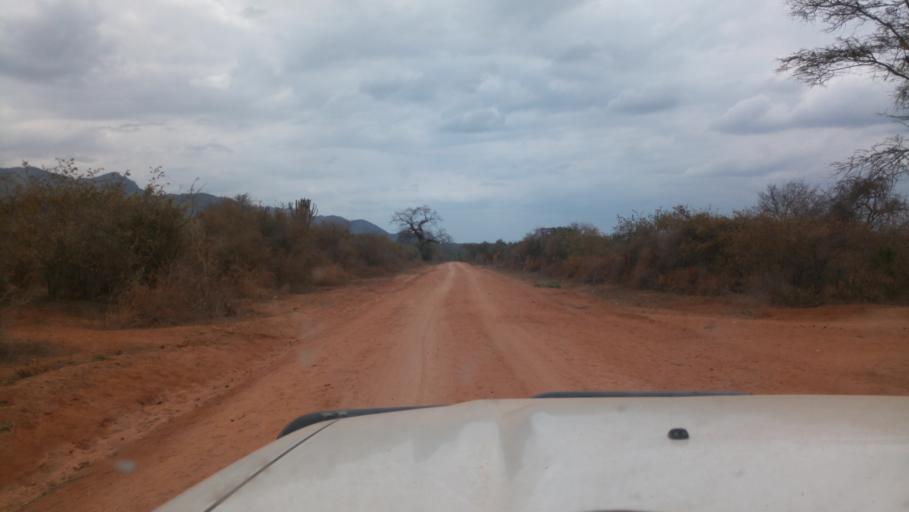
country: KE
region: Kitui
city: Kitui
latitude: -1.8260
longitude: 38.4274
